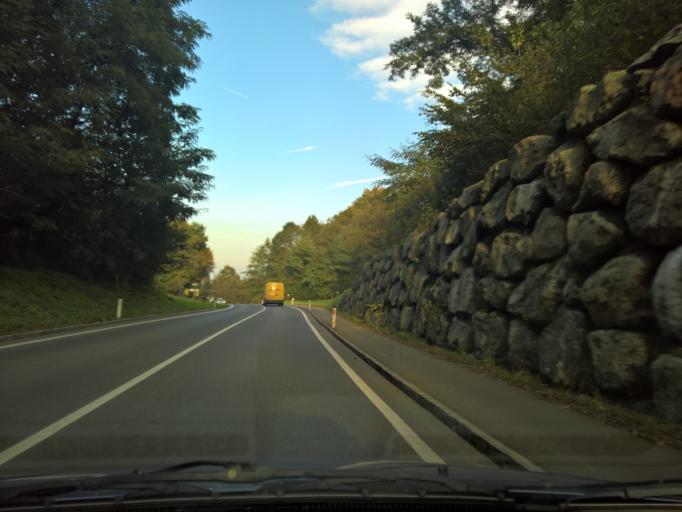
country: AT
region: Styria
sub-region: Politischer Bezirk Leibnitz
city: Grossklein
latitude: 46.7449
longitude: 15.4701
